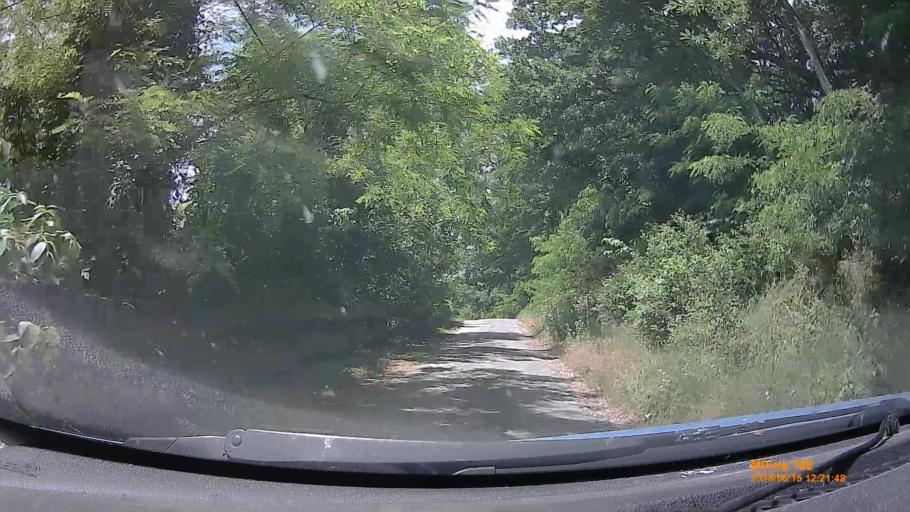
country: HU
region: Baranya
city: Buekkoesd
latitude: 46.1083
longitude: 18.0100
